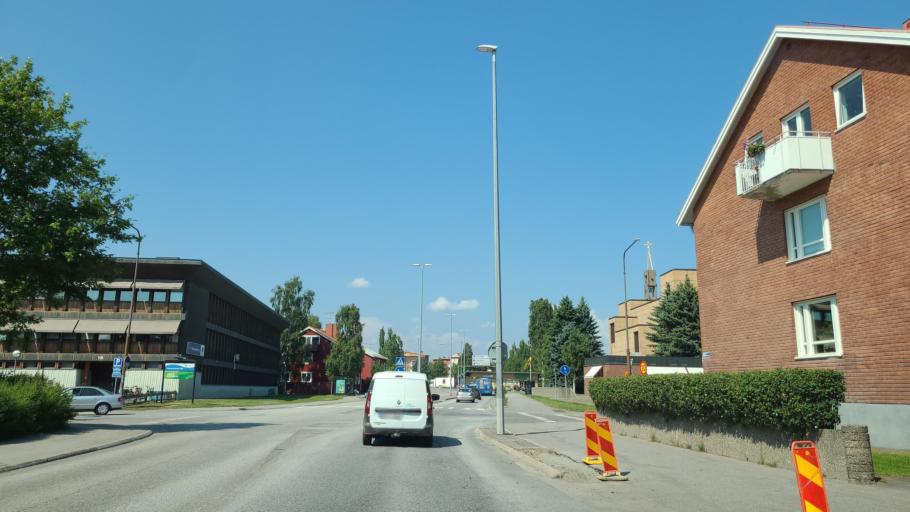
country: SE
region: Vaesterbotten
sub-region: Umea Kommun
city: Umea
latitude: 63.8184
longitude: 20.2558
